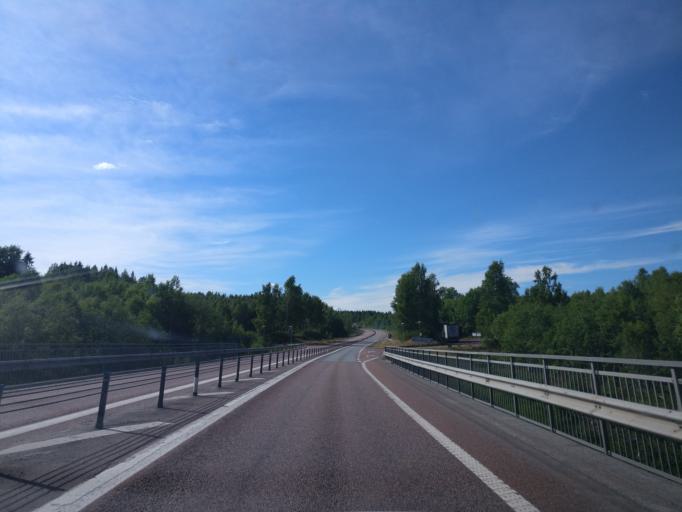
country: SE
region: Vaermland
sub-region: Kils Kommun
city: Kil
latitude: 59.5040
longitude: 13.2558
